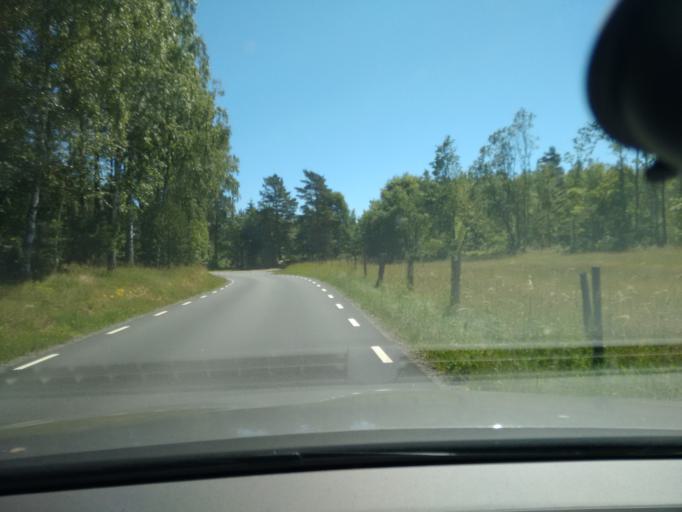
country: SE
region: Skane
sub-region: Kristianstads Kommun
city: Degeberga
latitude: 55.7736
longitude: 14.1264
